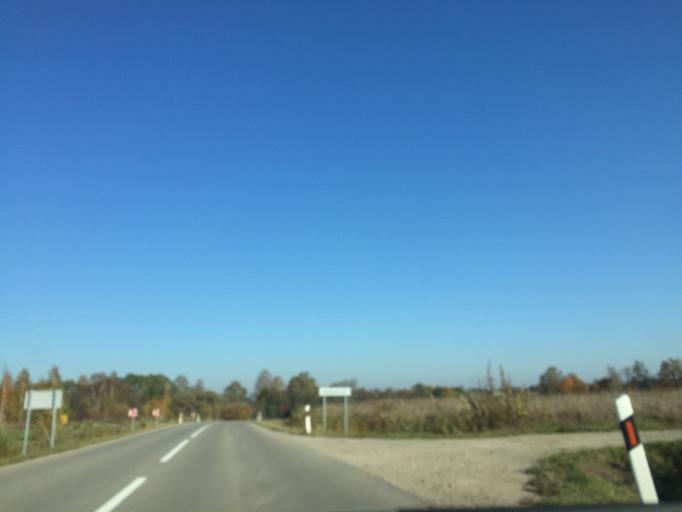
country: LT
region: Klaipedos apskritis
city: Kretinga
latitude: 55.7830
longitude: 21.2078
